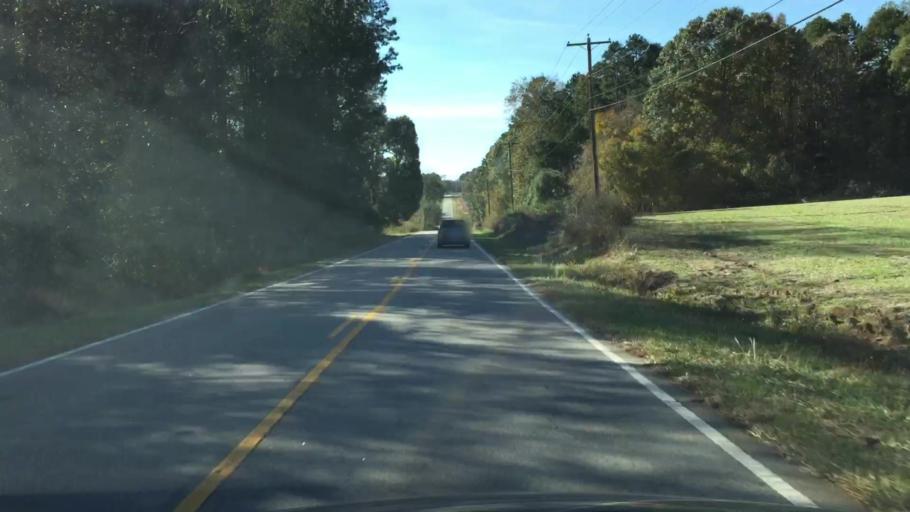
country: US
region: North Carolina
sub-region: Rowan County
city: China Grove
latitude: 35.6483
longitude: -80.6231
